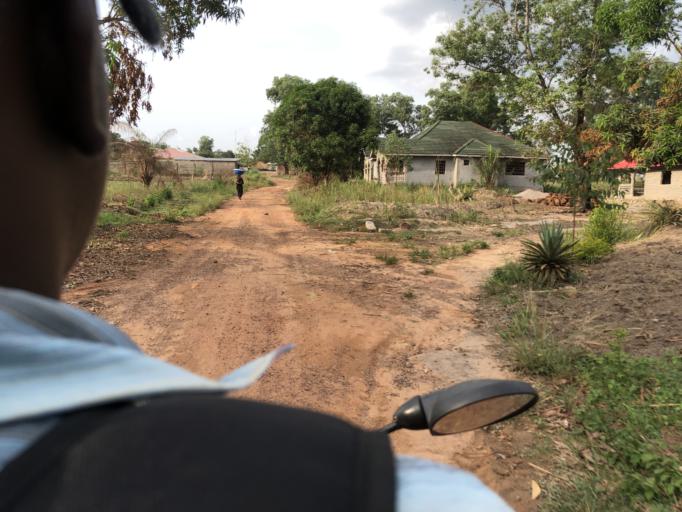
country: SL
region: Northern Province
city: Yonibana
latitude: 8.4577
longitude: -12.2030
